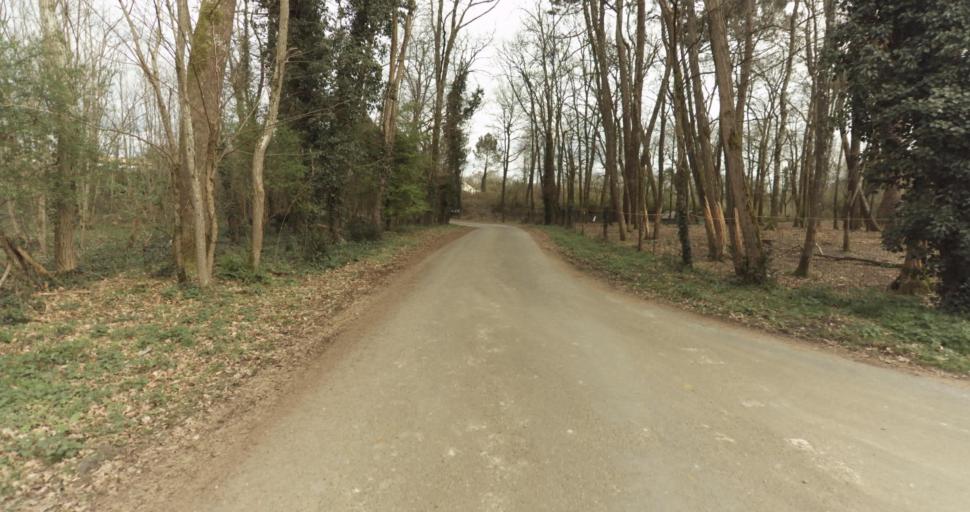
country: FR
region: Aquitaine
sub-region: Departement des Landes
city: Roquefort
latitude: 44.0427
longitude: -0.3242
